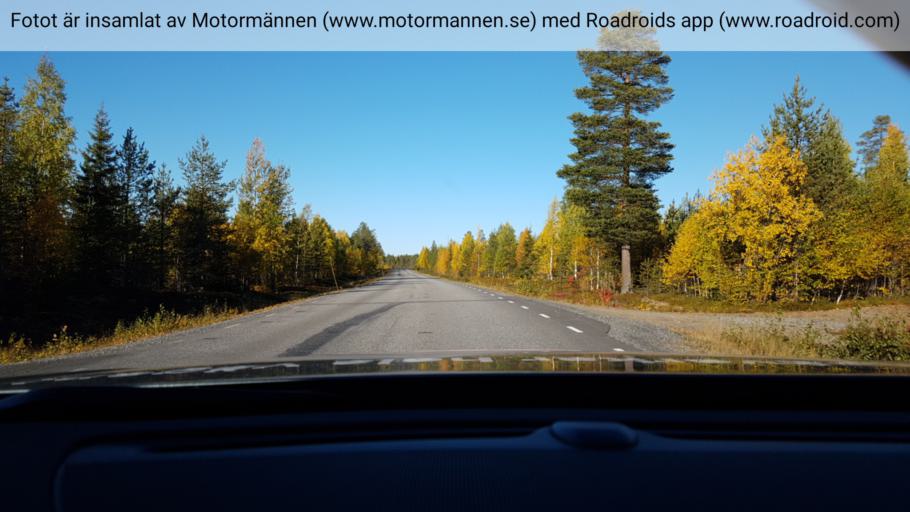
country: SE
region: Vaesterbotten
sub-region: Skelleftea Kommun
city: Storvik
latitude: 65.3283
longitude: 20.6671
